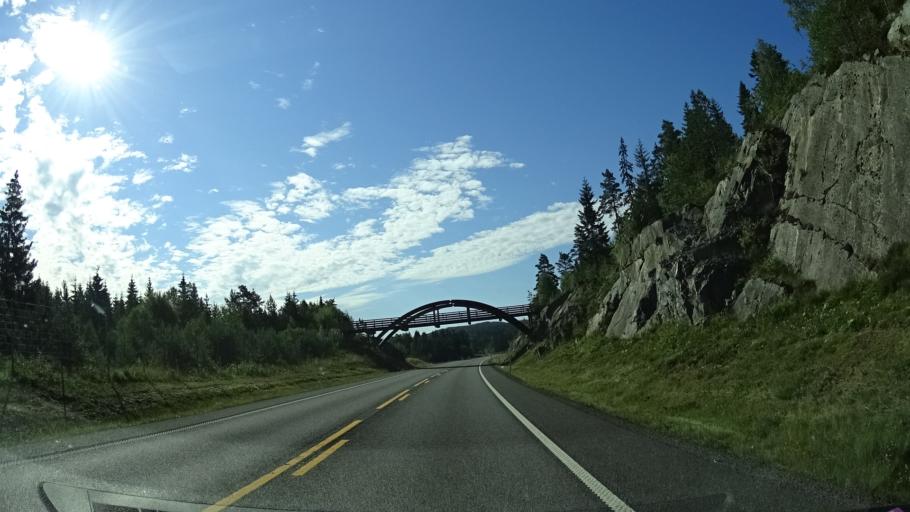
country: NO
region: Ostfold
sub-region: Marker
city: Orje
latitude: 59.5310
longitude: 11.5703
